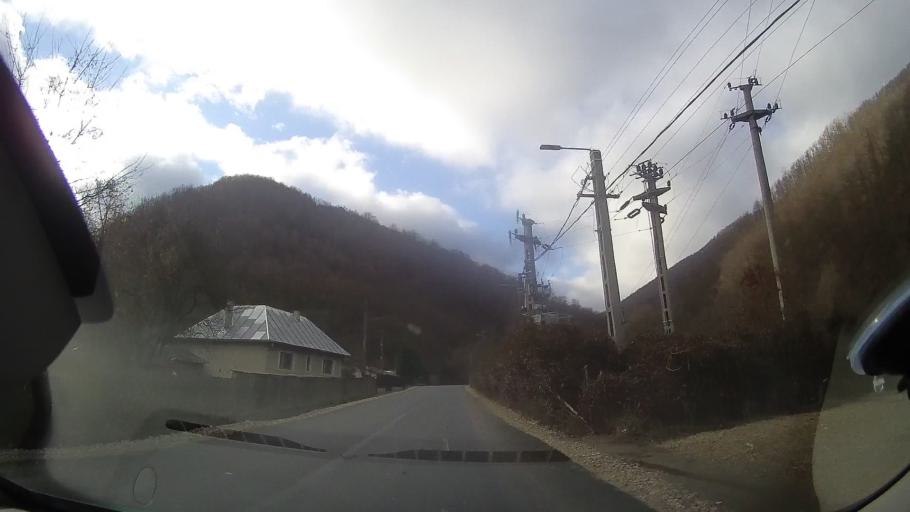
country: RO
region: Cluj
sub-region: Comuna Valea Ierii
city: Valea Ierii
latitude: 46.6914
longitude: 23.3072
